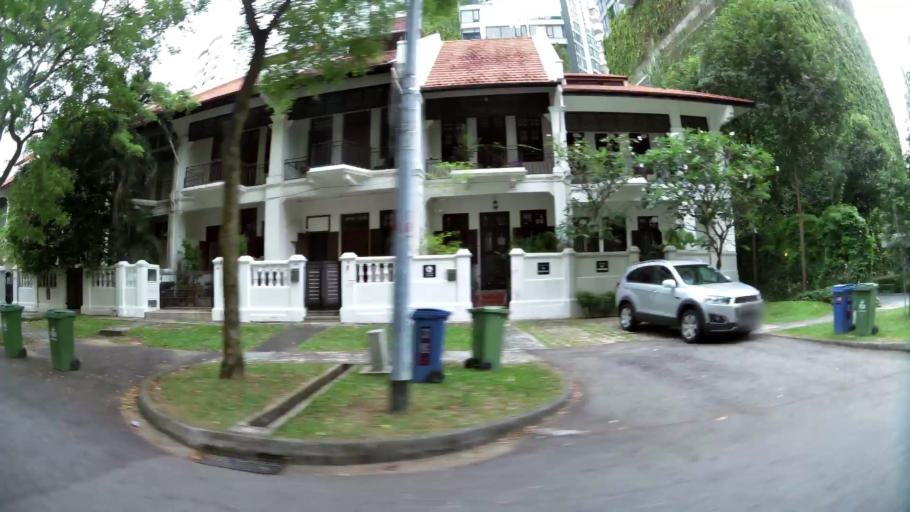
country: SG
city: Singapore
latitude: 1.3066
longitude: 103.8374
